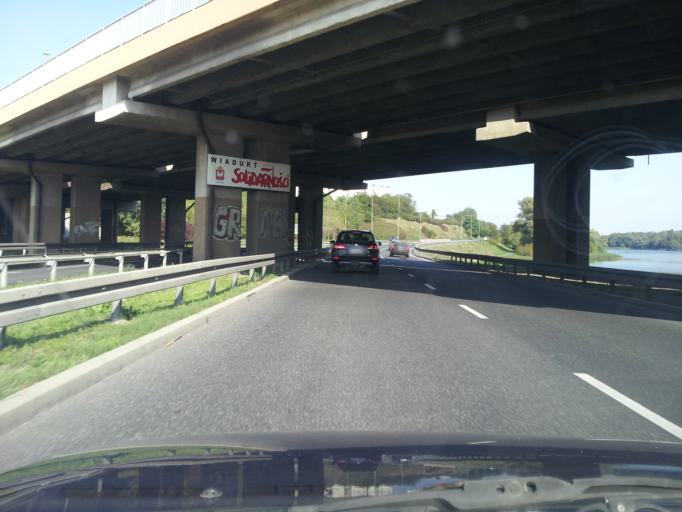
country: PL
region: Greater Poland Voivodeship
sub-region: Powiat gnieznienski
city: Gniezno
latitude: 52.5451
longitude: 17.6036
